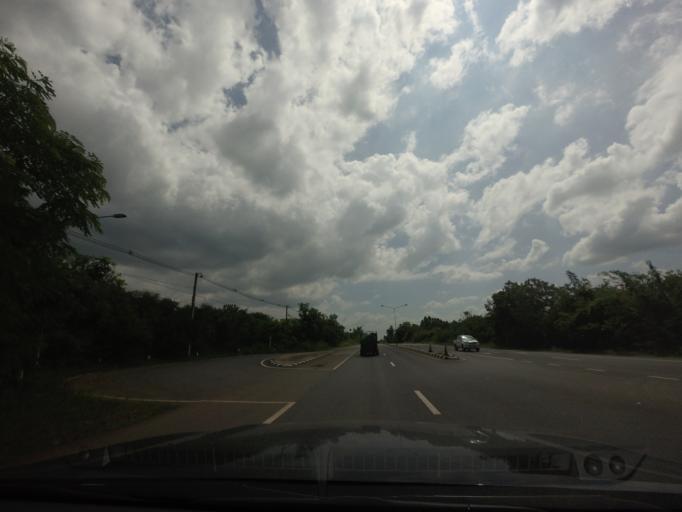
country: TH
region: Phetchabun
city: Phetchabun
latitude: 16.2133
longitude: 101.0890
